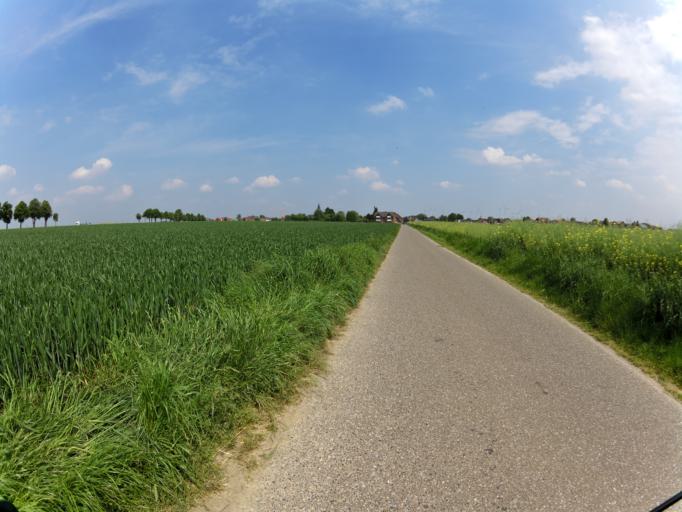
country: DE
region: North Rhine-Westphalia
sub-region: Regierungsbezirk Koln
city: Heinsberg
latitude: 51.0098
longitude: 6.0661
